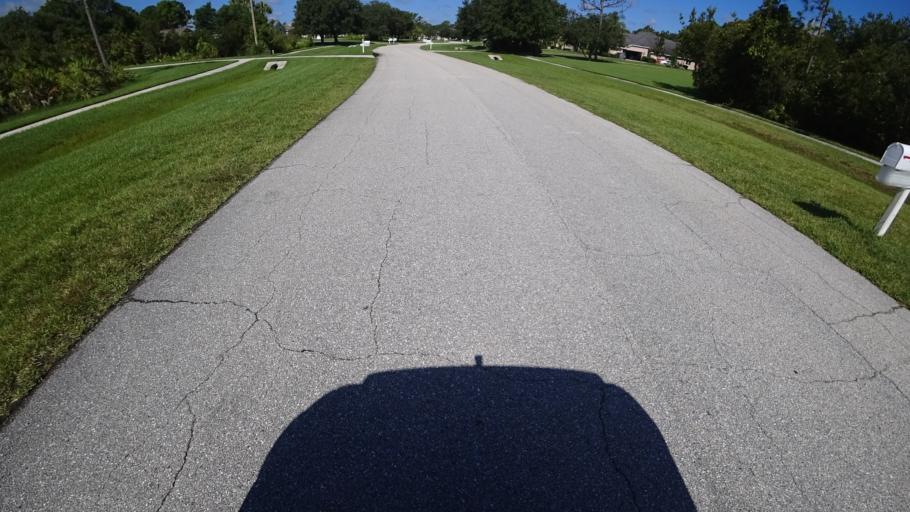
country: US
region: Florida
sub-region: Sarasota County
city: Fruitville
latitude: 27.3984
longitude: -82.3155
